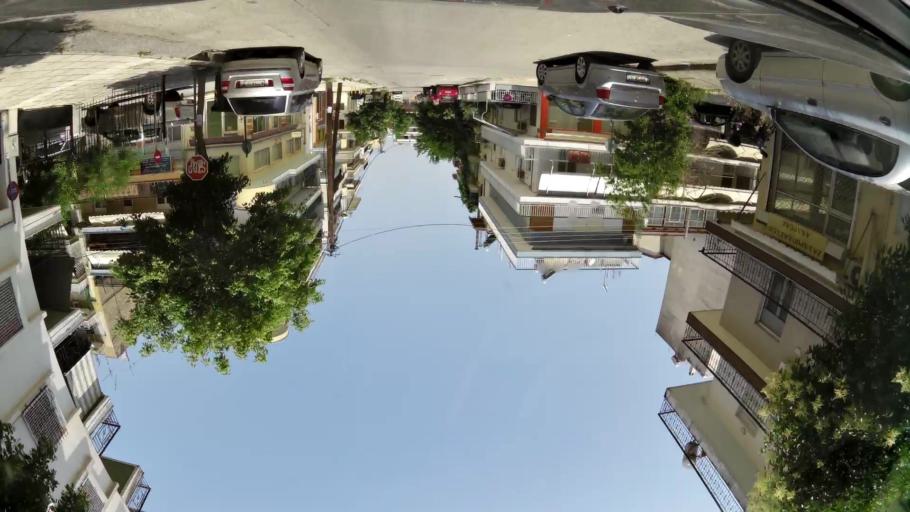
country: GR
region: Central Macedonia
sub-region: Nomos Thessalonikis
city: Evosmos
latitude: 40.6692
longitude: 22.8998
